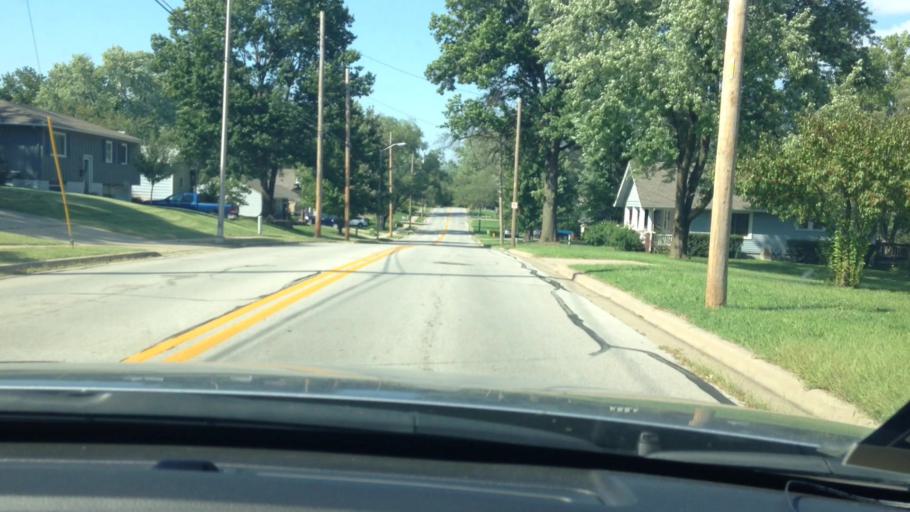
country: US
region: Kansas
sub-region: Johnson County
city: Shawnee
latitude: 39.0189
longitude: -94.7308
